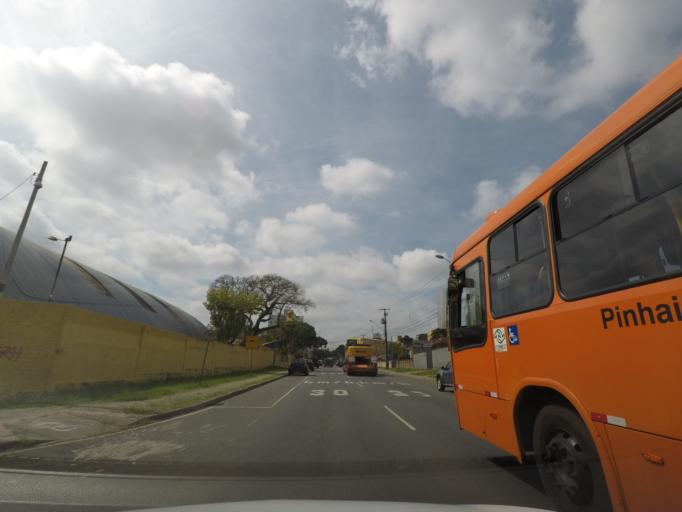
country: BR
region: Parana
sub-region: Curitiba
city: Curitiba
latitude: -25.4794
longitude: -49.3000
